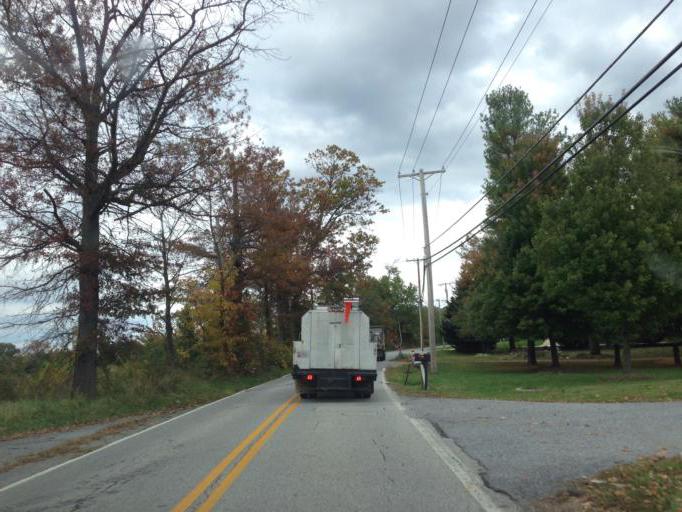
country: US
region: Maryland
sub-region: Baltimore County
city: Milford Mill
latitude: 39.3152
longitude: -76.7753
